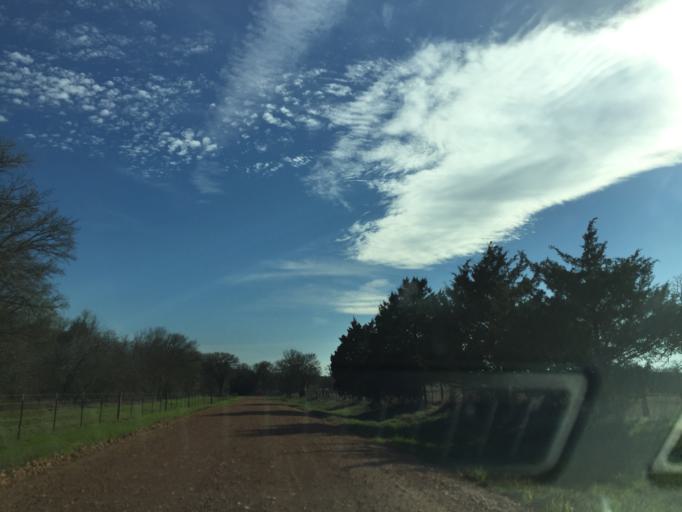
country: US
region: Texas
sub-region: Milam County
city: Thorndale
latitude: 30.4501
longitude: -97.1774
